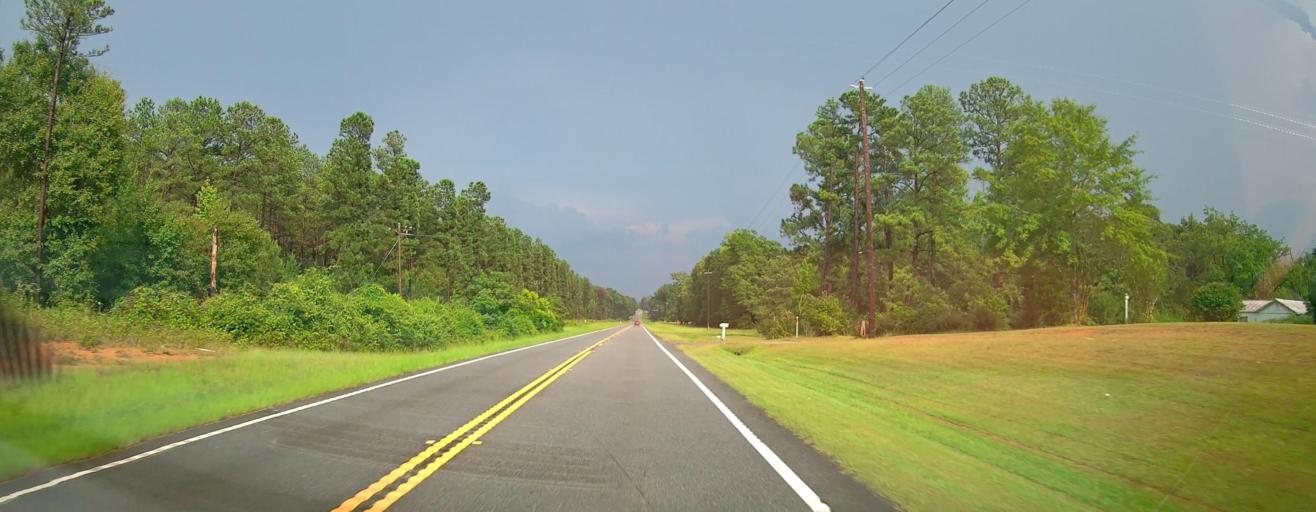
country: US
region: Georgia
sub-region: Twiggs County
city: Jeffersonville
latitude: 32.6079
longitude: -83.2655
